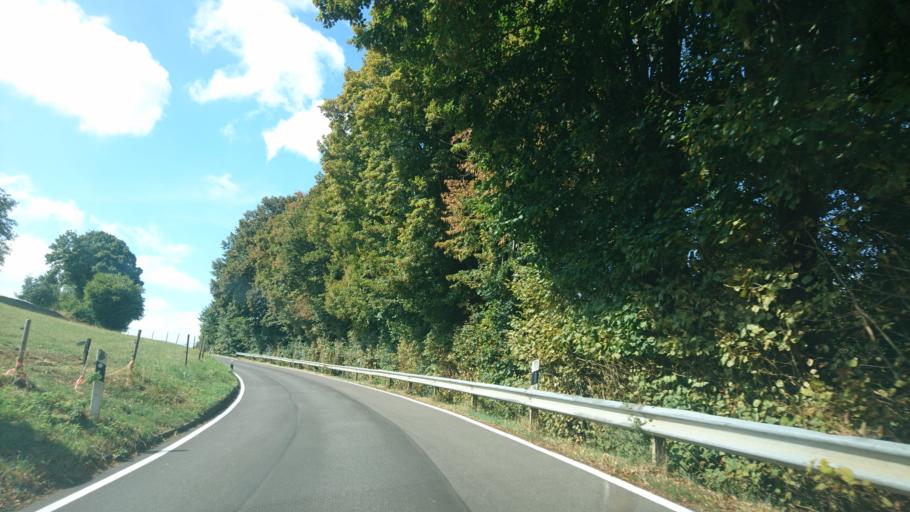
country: DE
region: Rheinland-Pfalz
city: Merzkirchen
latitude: 49.5793
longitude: 6.4886
